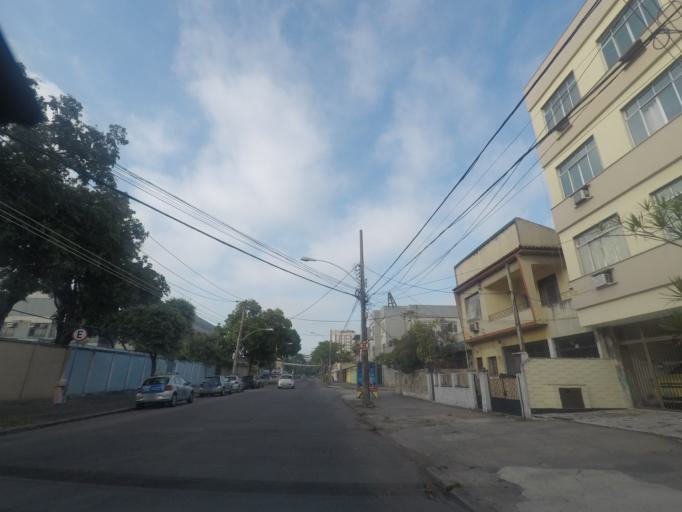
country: BR
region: Rio de Janeiro
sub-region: Duque De Caxias
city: Duque de Caxias
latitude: -22.8395
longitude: -43.2663
